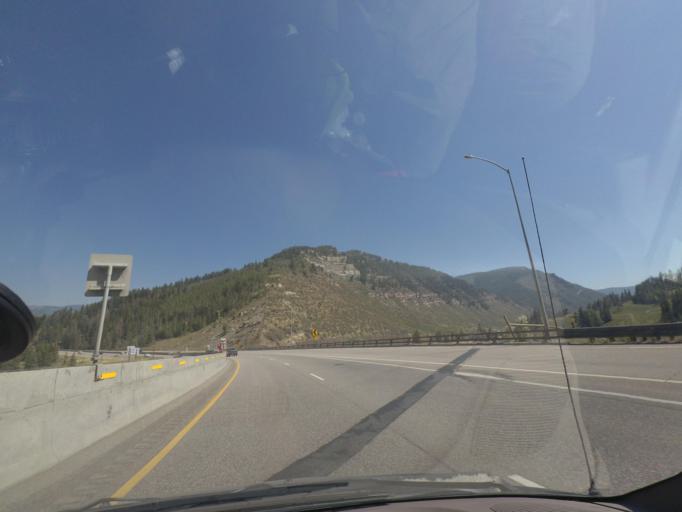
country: US
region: Colorado
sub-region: Eagle County
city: Minturn
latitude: 39.6080
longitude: -106.4494
